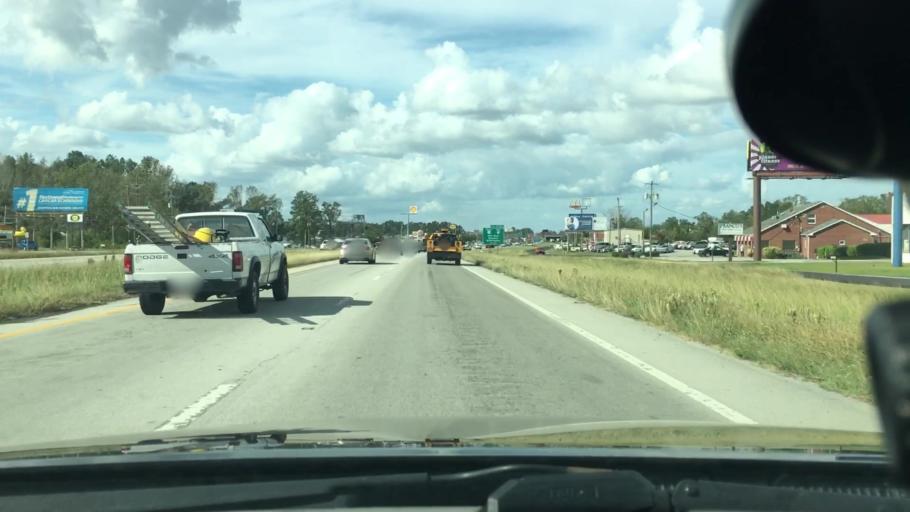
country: US
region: North Carolina
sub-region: Craven County
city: James City
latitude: 35.0774
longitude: -77.0293
